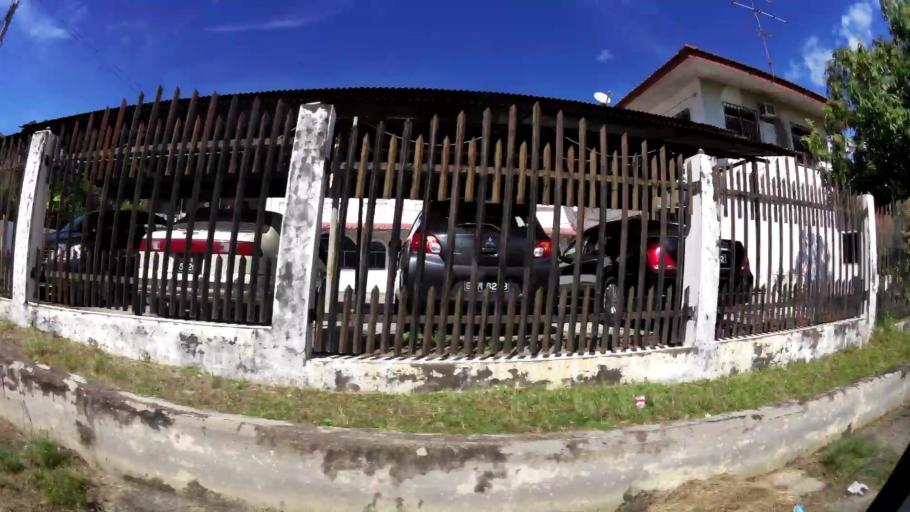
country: BN
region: Brunei and Muara
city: Bandar Seri Begawan
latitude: 4.9556
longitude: 114.9453
